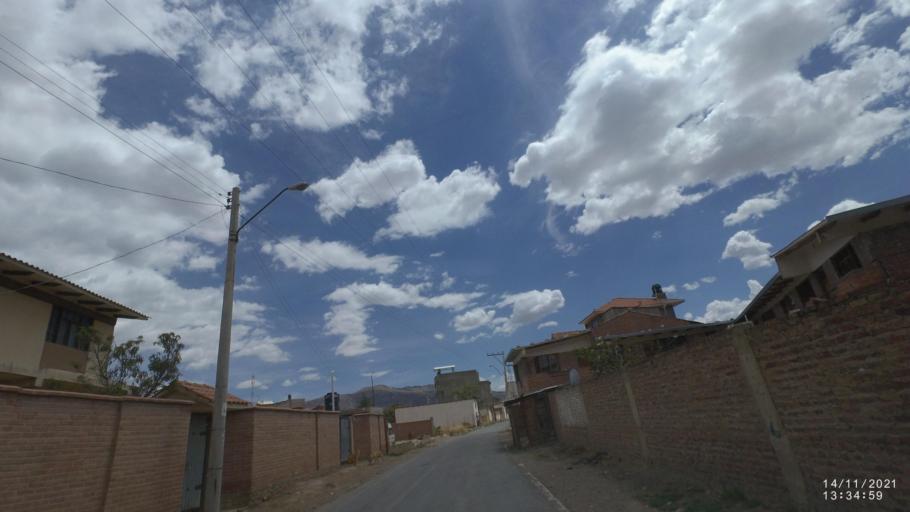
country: BO
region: Cochabamba
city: Colomi
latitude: -17.4057
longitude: -65.9863
